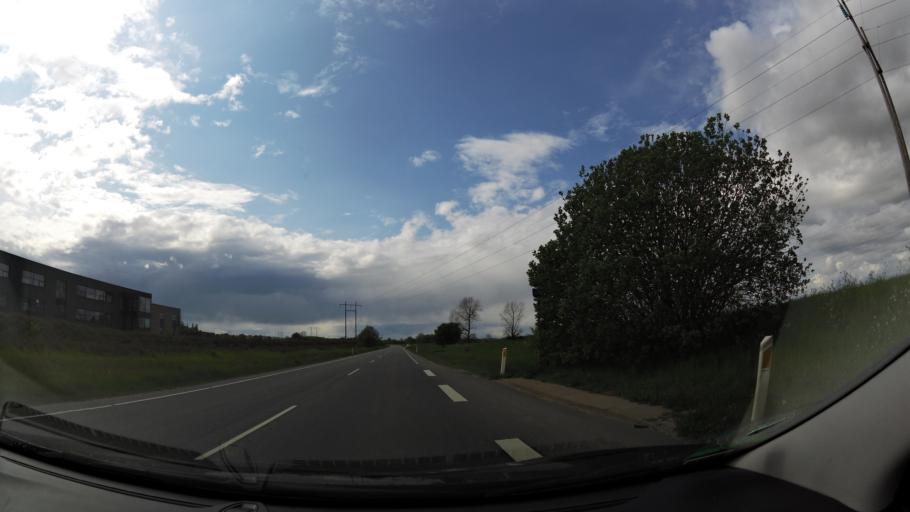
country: DK
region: South Denmark
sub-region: Nyborg Kommune
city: Nyborg
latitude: 55.3175
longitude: 10.7490
